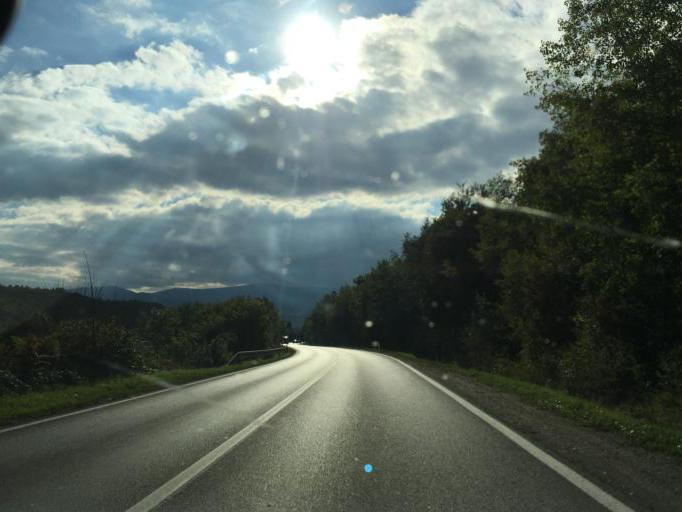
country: BA
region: Federation of Bosnia and Herzegovina
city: Bugojno
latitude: 44.0716
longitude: 17.4963
